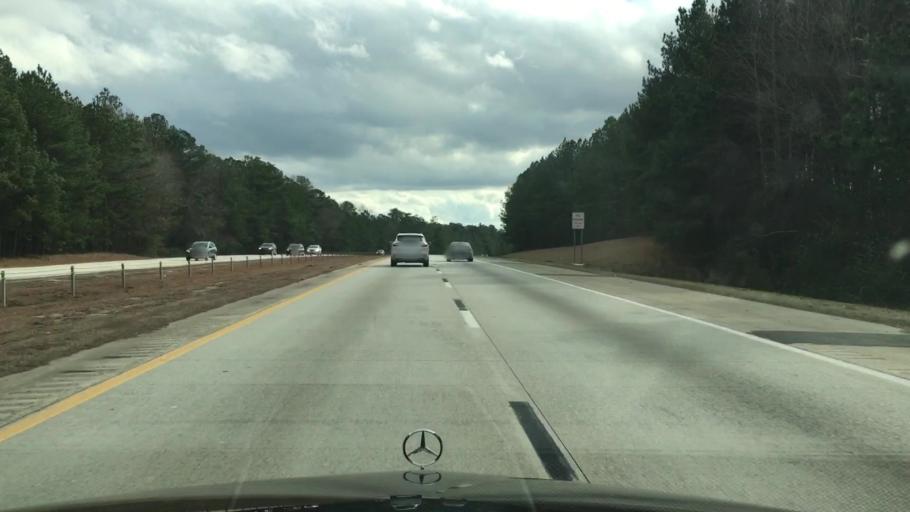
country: US
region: North Carolina
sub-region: Wake County
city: Garner
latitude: 35.6804
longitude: -78.5664
